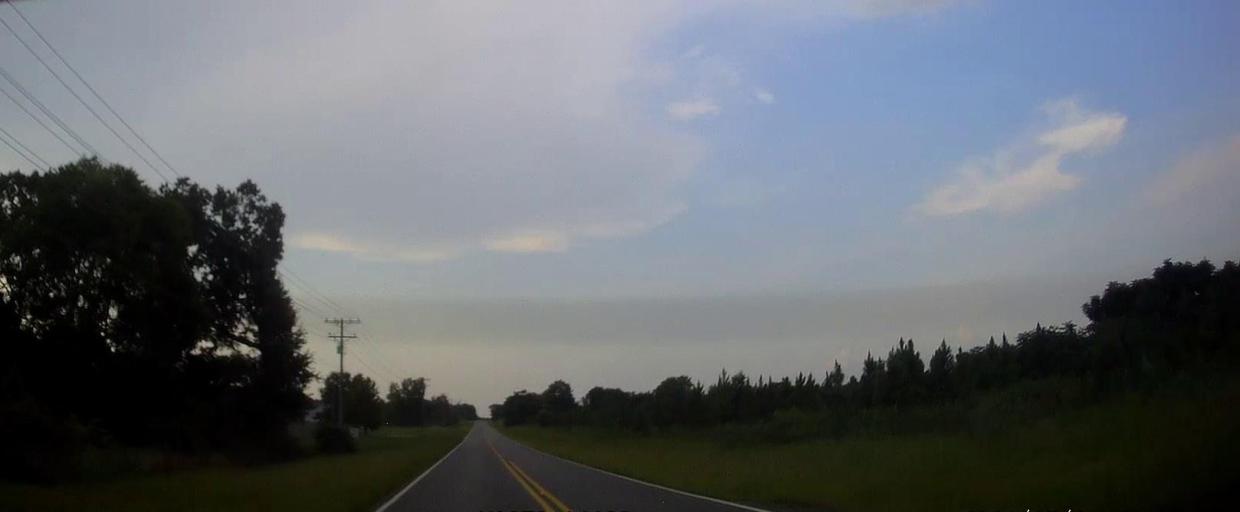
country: US
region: Georgia
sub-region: Laurens County
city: East Dublin
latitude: 32.5476
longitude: -82.8370
